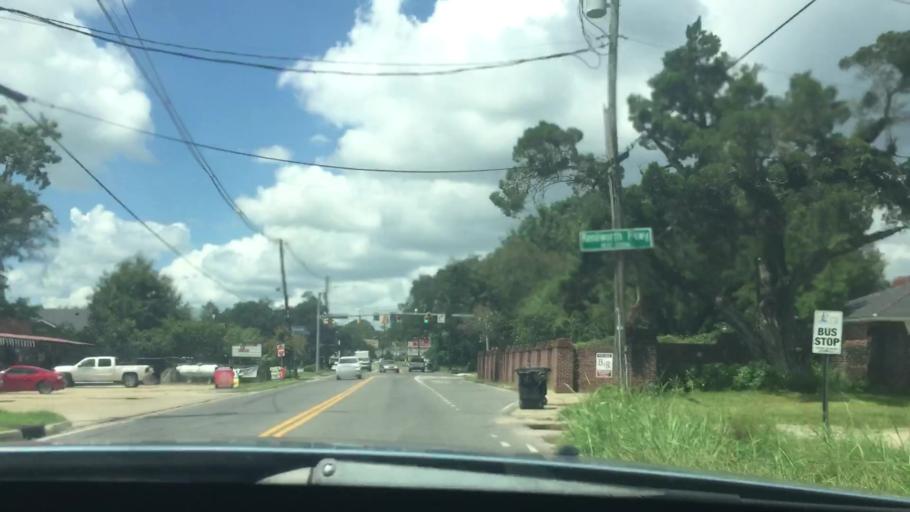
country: US
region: Louisiana
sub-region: East Baton Rouge Parish
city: Gardere
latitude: 30.3752
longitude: -91.1349
